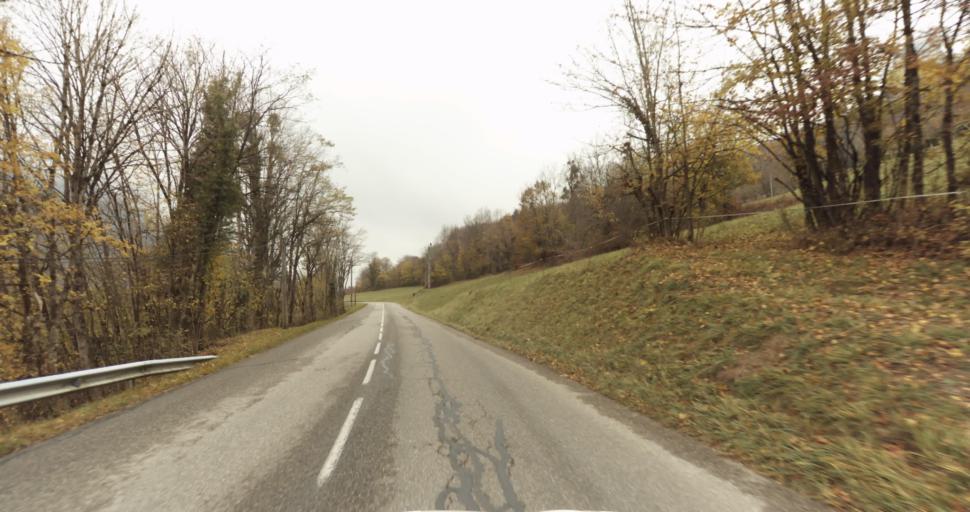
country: FR
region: Rhone-Alpes
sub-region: Departement de la Haute-Savoie
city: Gruffy
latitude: 45.7543
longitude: 6.0738
